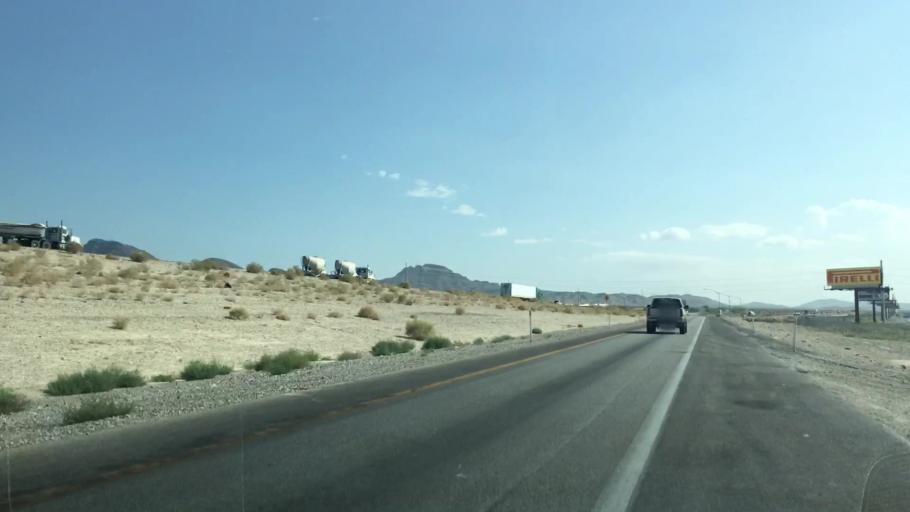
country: US
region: Nevada
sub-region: Clark County
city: Nellis Air Force Base
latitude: 36.2823
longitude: -115.0242
